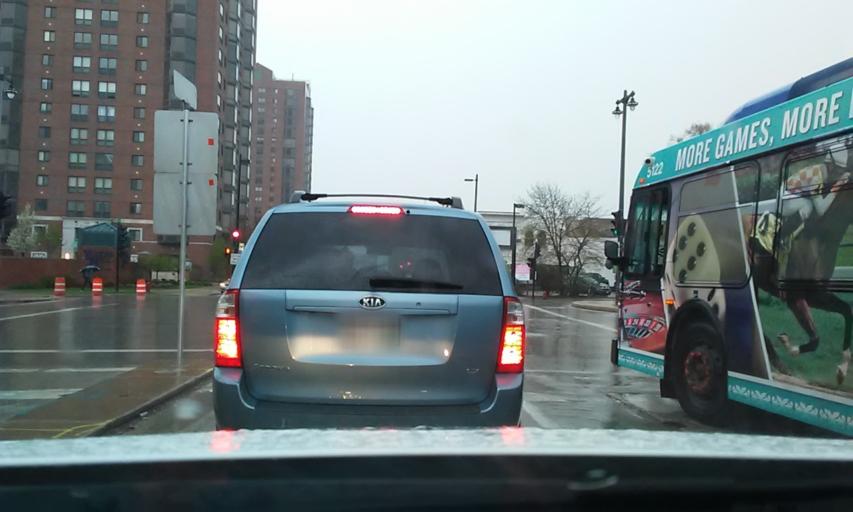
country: US
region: Wisconsin
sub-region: Milwaukee County
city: Milwaukee
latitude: 43.0427
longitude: -87.9032
